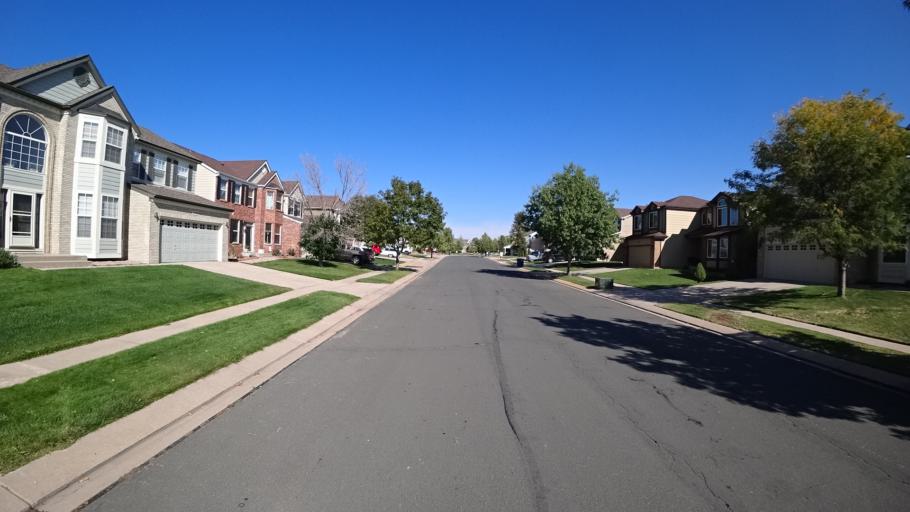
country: US
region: Colorado
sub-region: El Paso County
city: Cimarron Hills
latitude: 38.8825
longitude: -104.7082
